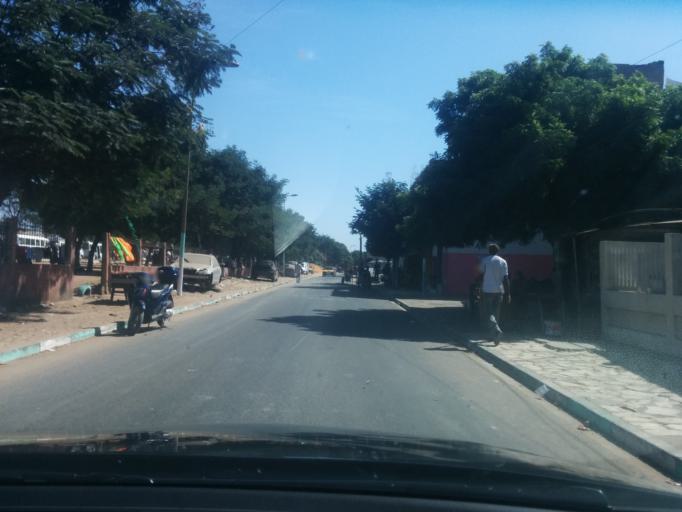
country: SN
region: Dakar
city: Grand Dakar
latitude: 14.7427
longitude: -17.4436
